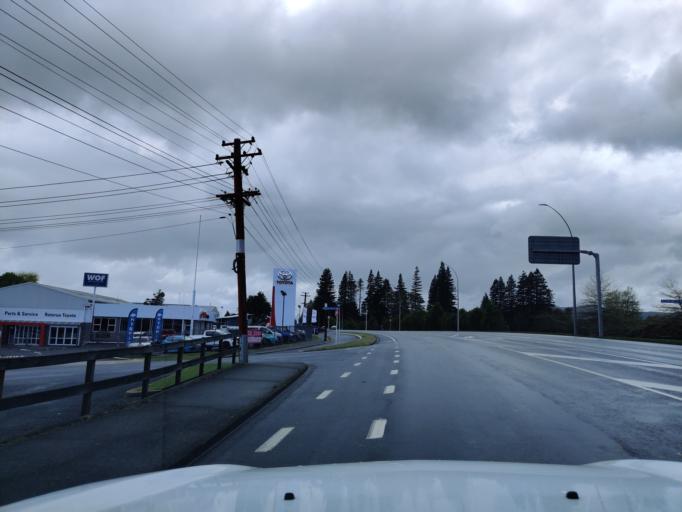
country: NZ
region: Bay of Plenty
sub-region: Rotorua District
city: Rotorua
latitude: -38.1469
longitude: 176.2789
